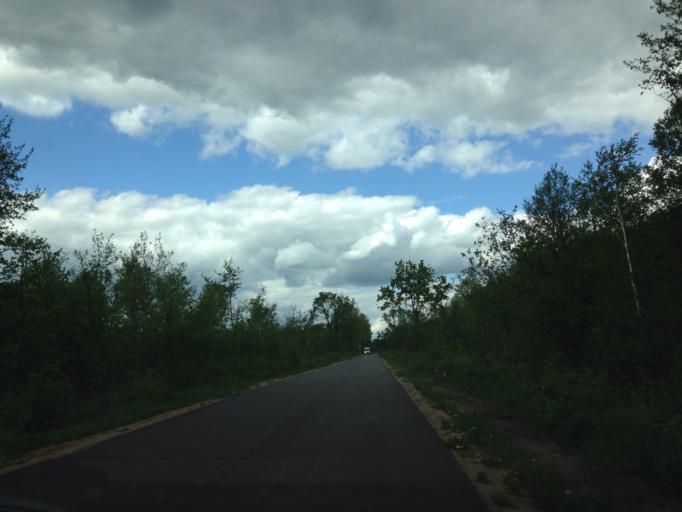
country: PL
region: Podlasie
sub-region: Powiat bialostocki
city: Tykocin
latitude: 53.3048
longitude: 22.6041
